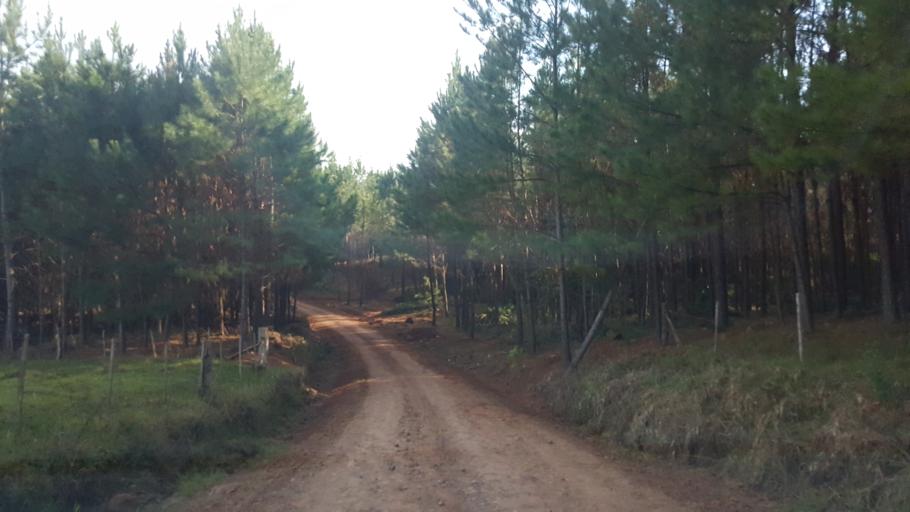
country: AR
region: Misiones
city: Capiovi
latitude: -26.9039
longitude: -55.0911
